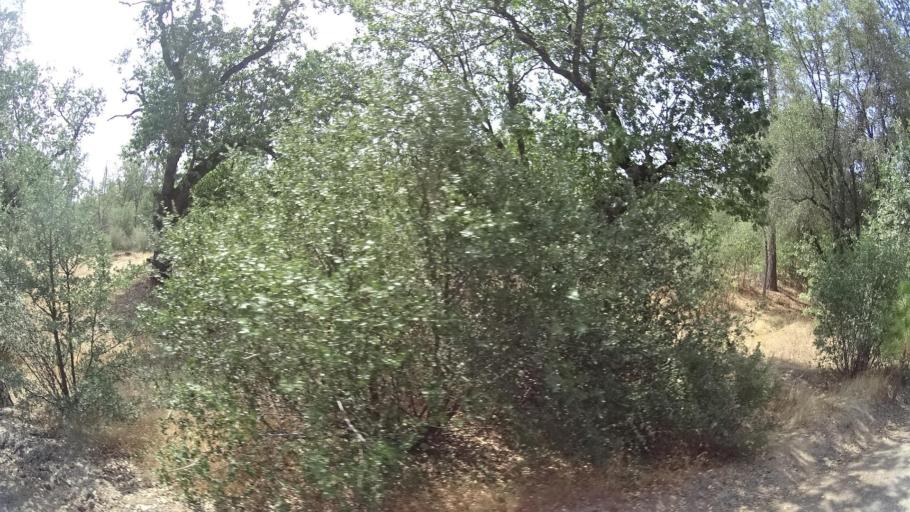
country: US
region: California
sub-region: Mariposa County
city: Midpines
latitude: 37.6951
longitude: -120.1043
